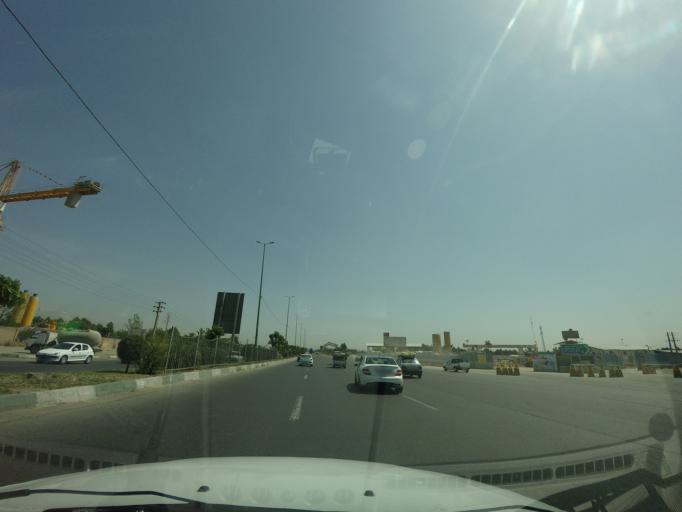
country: IR
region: Tehran
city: Eslamshahr
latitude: 35.6189
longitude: 51.3221
